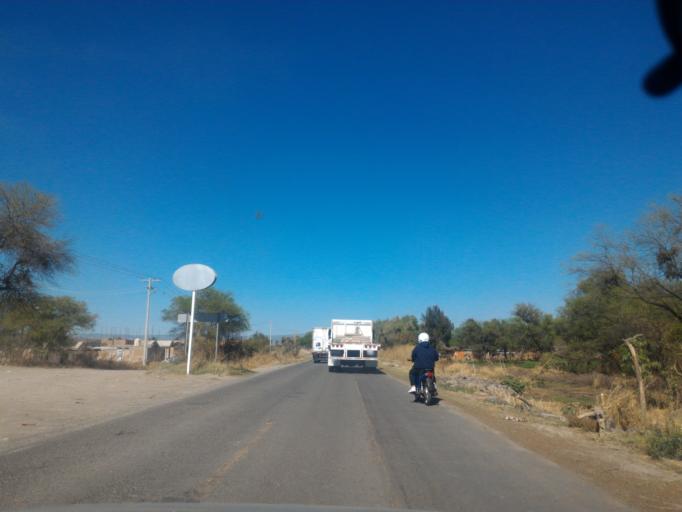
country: MX
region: Guanajuato
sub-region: Leon
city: Malagana (San Antonio del Monte)
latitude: 21.0342
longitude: -101.7746
